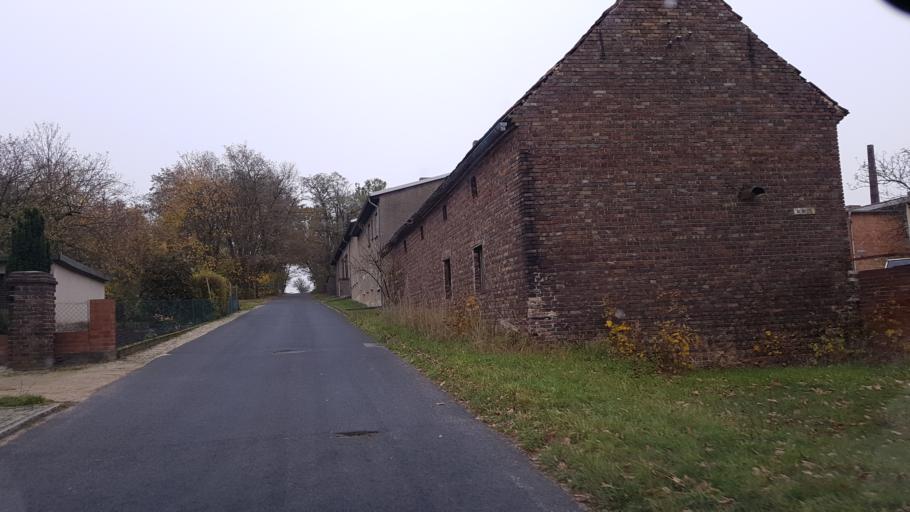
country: DE
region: Brandenburg
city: Crinitz
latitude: 51.7365
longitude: 13.7607
